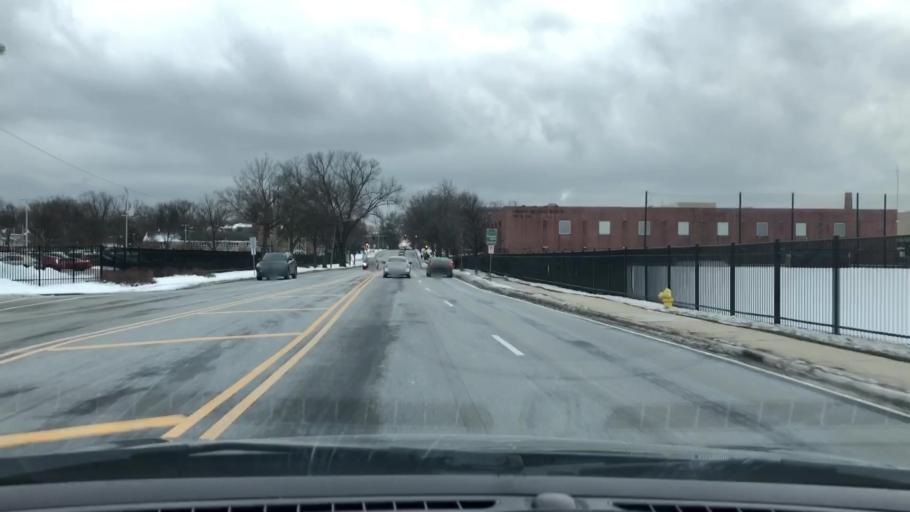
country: US
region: Illinois
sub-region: DuPage County
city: Downers Grove
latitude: 41.8076
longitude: -88.0111
